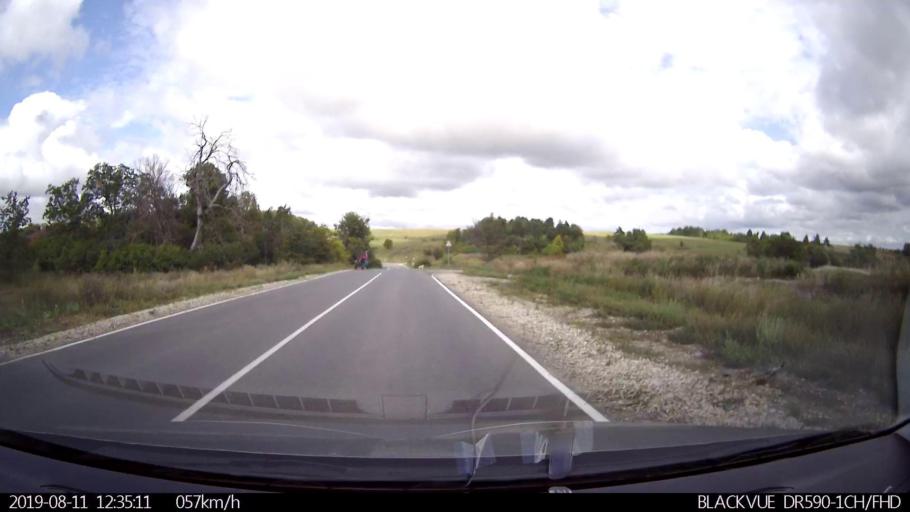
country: RU
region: Ulyanovsk
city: Ignatovka
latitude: 53.8227
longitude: 47.8345
